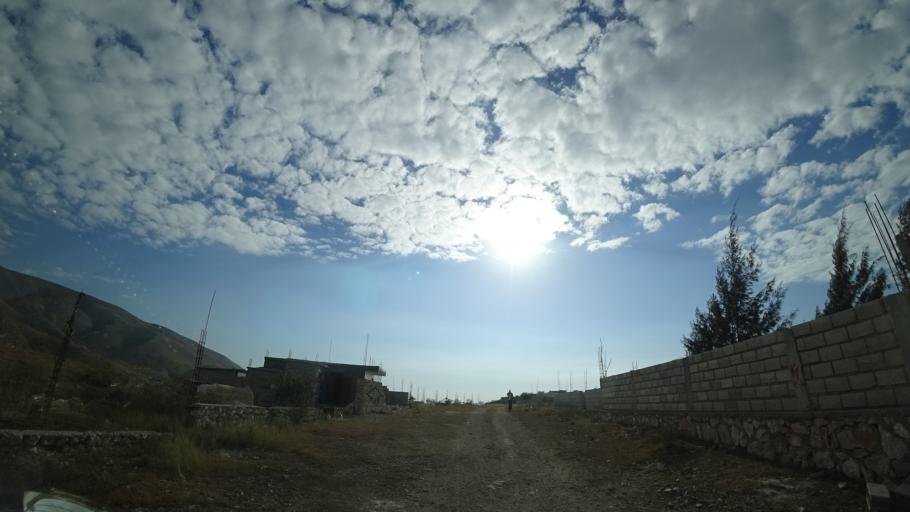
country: HT
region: Ouest
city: Croix des Bouquets
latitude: 18.6759
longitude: -72.2931
